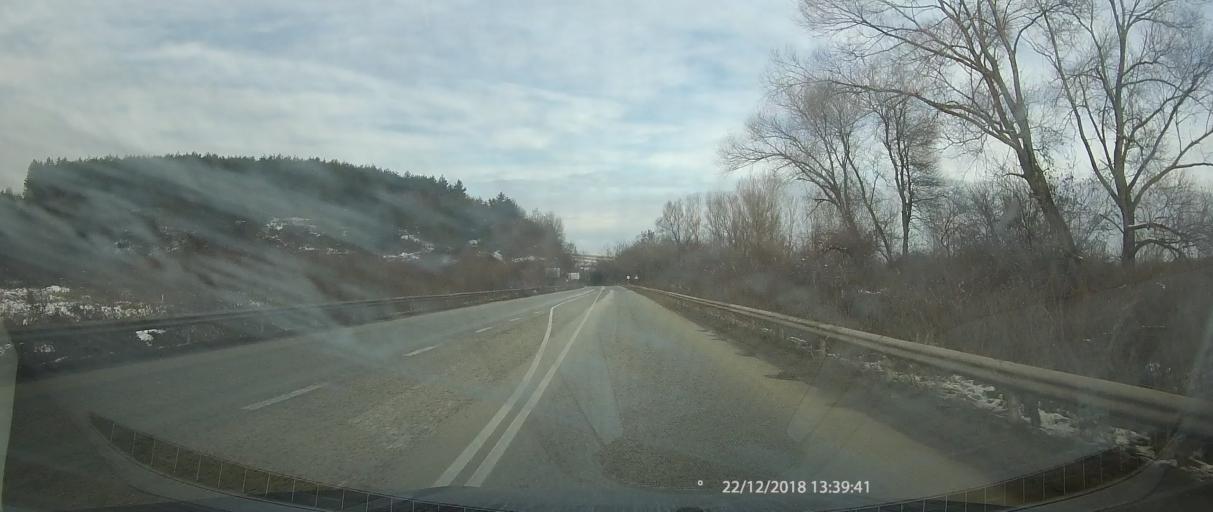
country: BG
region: Lovech
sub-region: Obshtina Lukovit
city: Lukovit
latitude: 43.1676
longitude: 24.1476
